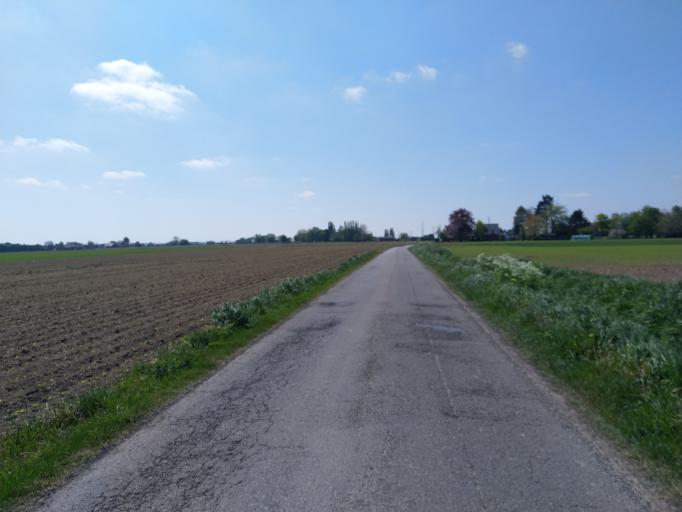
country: BE
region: Wallonia
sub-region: Province du Hainaut
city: Lens
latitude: 50.5399
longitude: 3.8514
